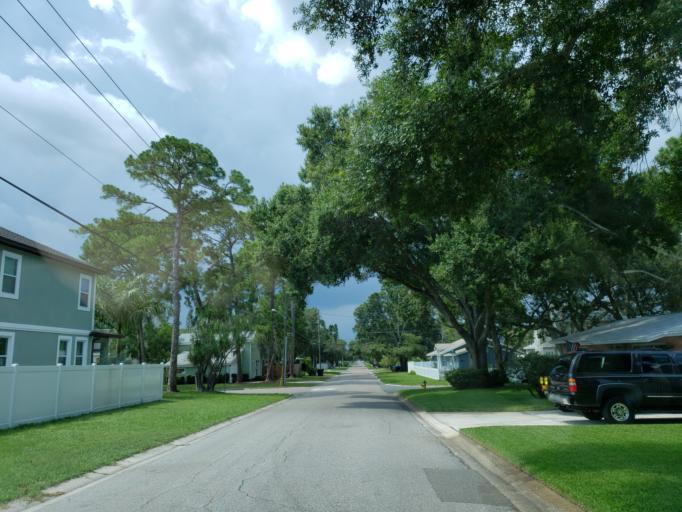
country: US
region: Florida
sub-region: Pinellas County
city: Lealman
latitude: 27.8017
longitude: -82.6406
